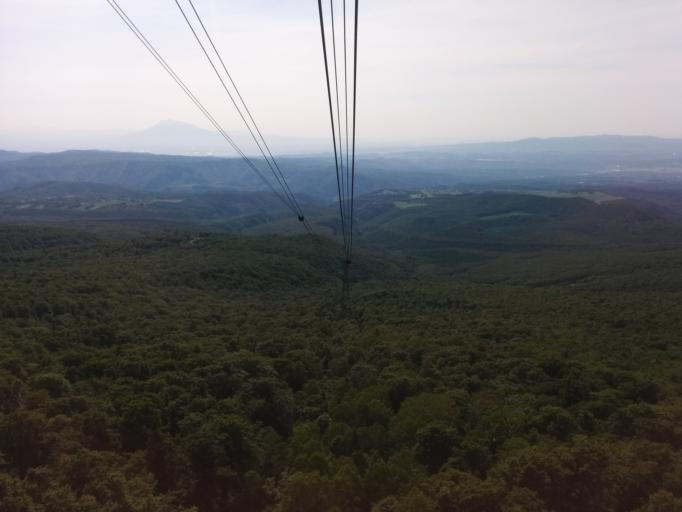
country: JP
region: Aomori
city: Aomori Shi
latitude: 40.6772
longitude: 140.8515
